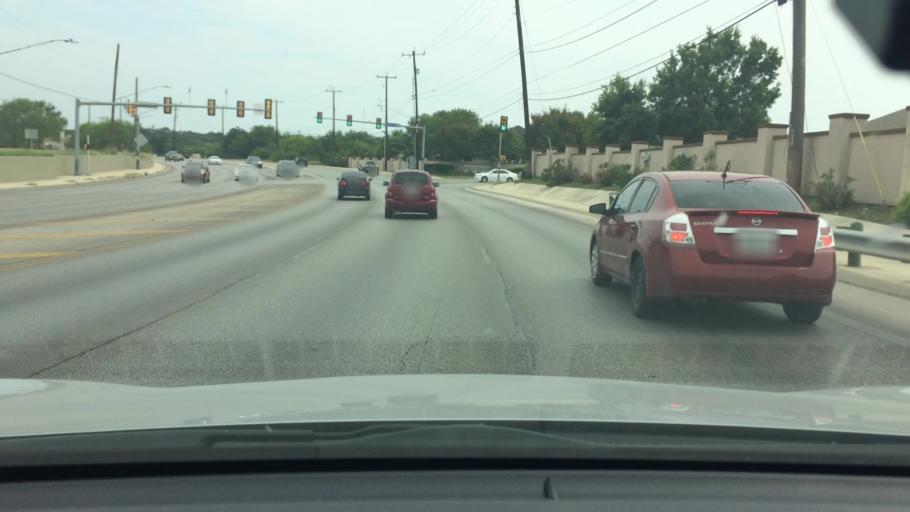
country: US
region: Texas
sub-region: Bexar County
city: Leon Valley
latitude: 29.4819
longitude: -98.6674
